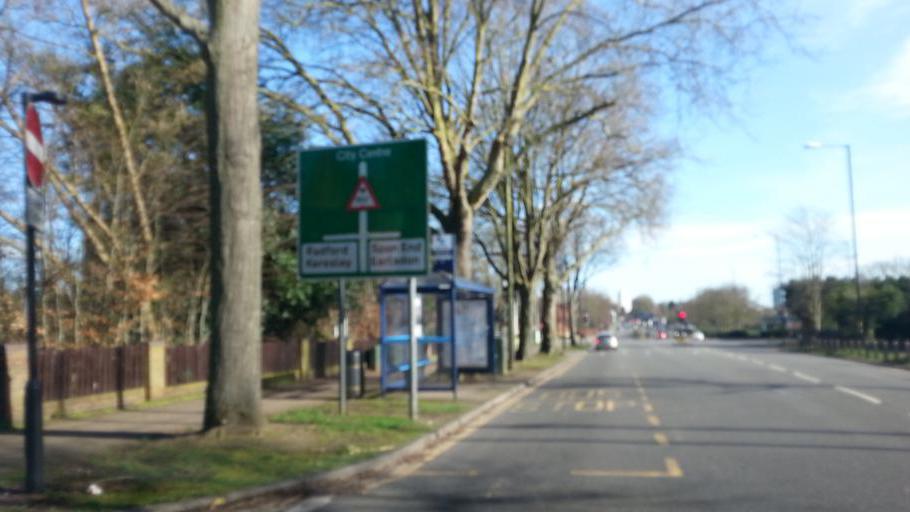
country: GB
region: England
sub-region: Coventry
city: Coventry
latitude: 52.4145
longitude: -1.5332
